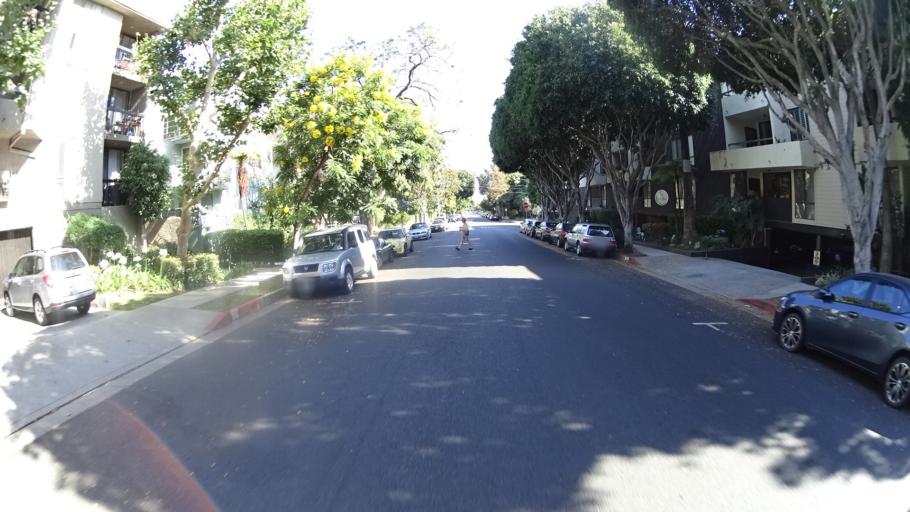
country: US
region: California
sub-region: Los Angeles County
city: West Hollywood
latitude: 34.0876
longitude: -118.3717
